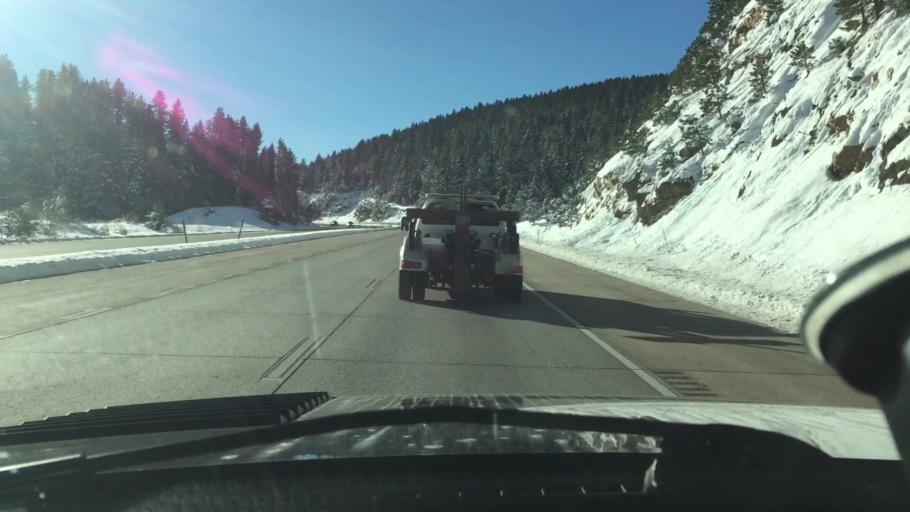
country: US
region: Colorado
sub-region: Jefferson County
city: Indian Hills
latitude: 39.6045
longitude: -105.2293
